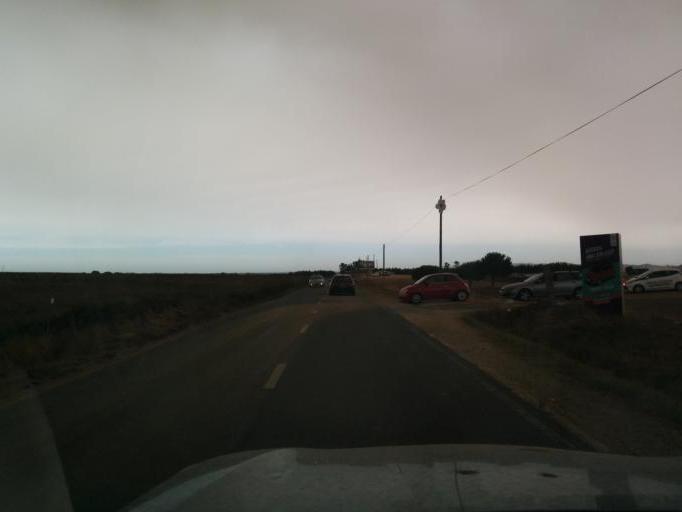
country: PT
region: Beja
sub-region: Odemira
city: Sao Teotonio
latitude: 37.5517
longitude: -8.7344
